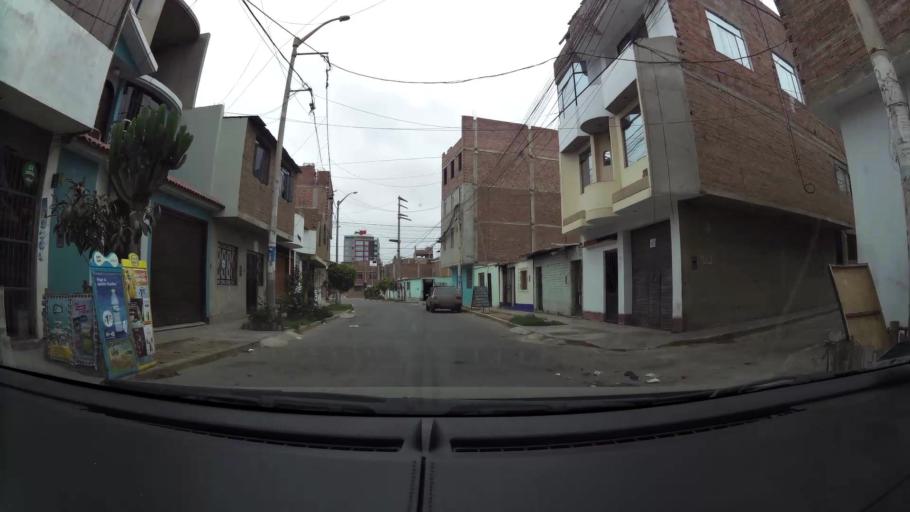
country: PE
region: La Libertad
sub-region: Provincia de Trujillo
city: Trujillo
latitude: -8.1231
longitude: -79.0266
